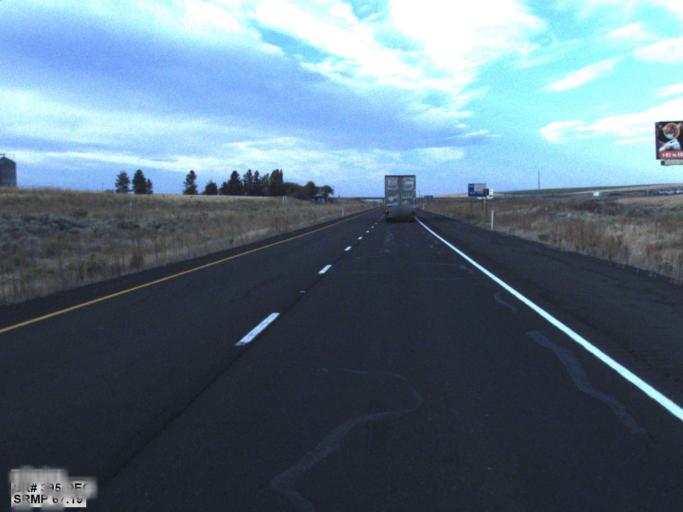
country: US
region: Washington
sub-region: Franklin County
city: Connell
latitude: 46.7992
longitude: -118.7359
